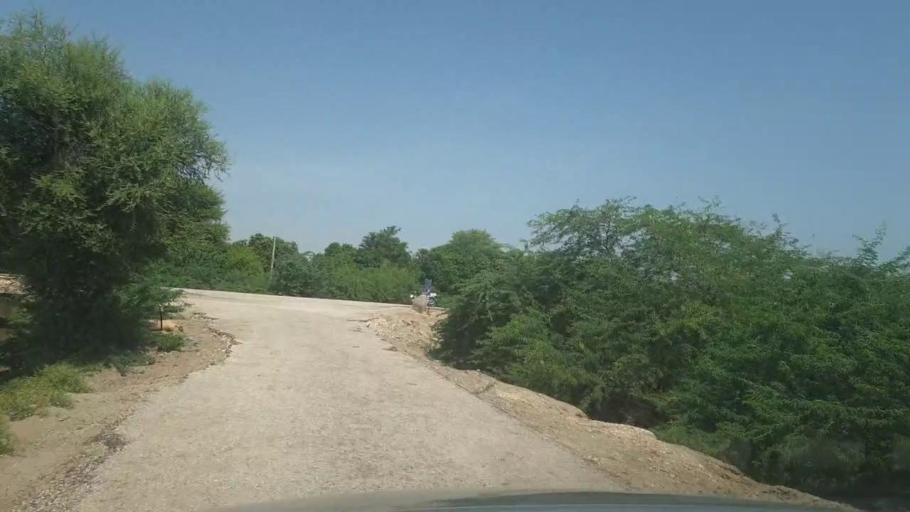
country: PK
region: Sindh
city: Khairpur
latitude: 27.4042
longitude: 69.0349
